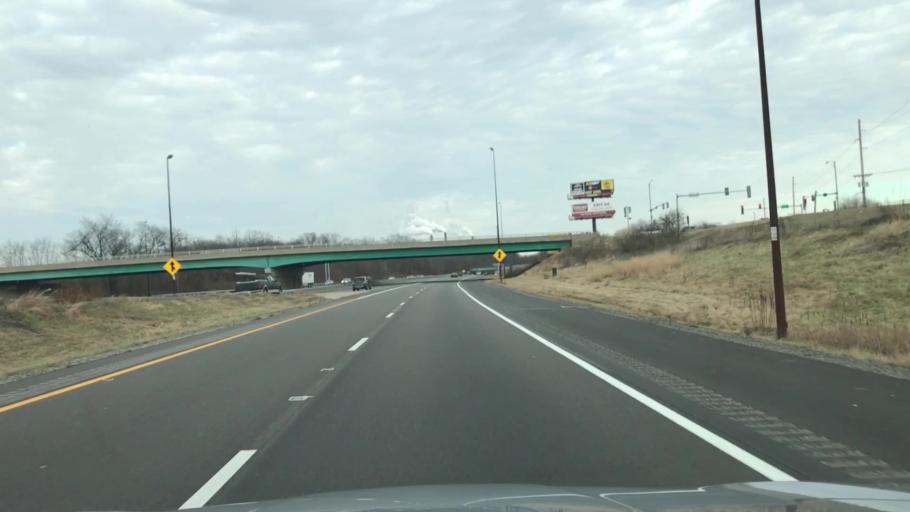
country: US
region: Illinois
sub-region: Sangamon County
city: Southern View
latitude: 39.7428
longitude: -89.6374
